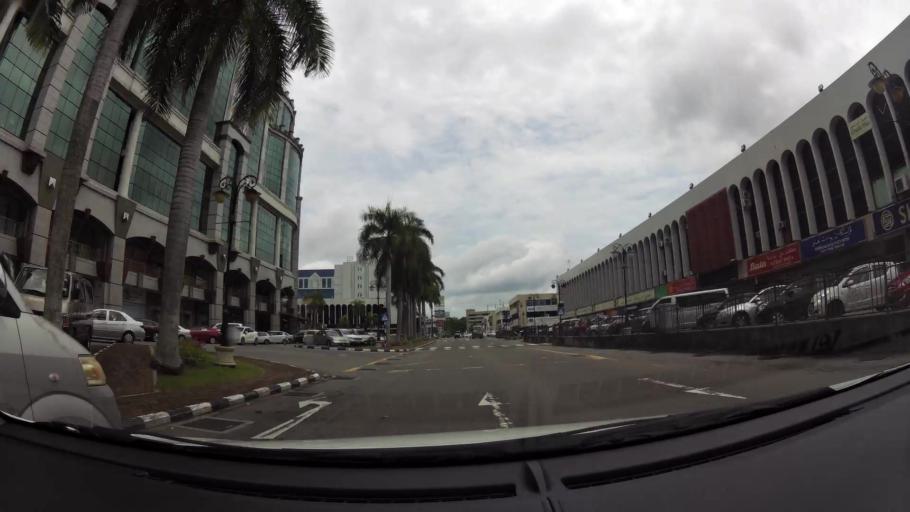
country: BN
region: Brunei and Muara
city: Bandar Seri Begawan
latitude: 4.9061
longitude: 114.9173
